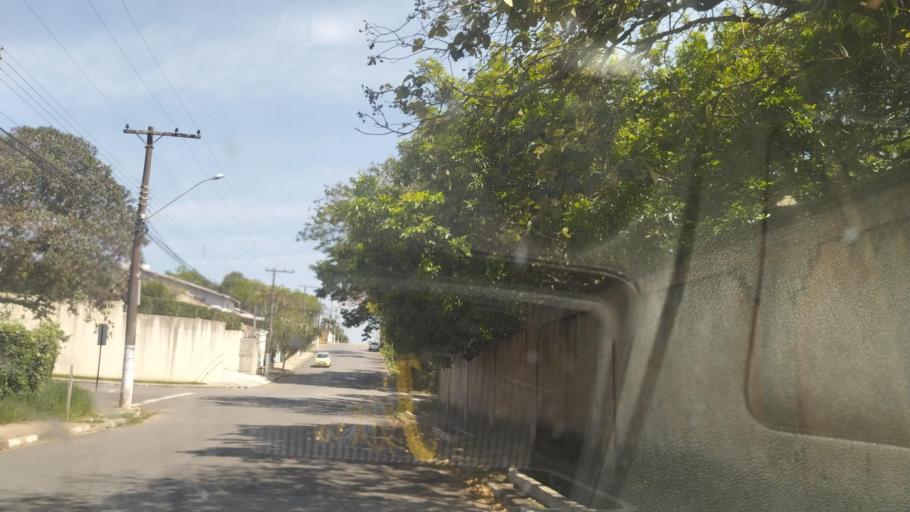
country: BR
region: Sao Paulo
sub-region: Atibaia
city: Atibaia
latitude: -23.1266
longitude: -46.5453
